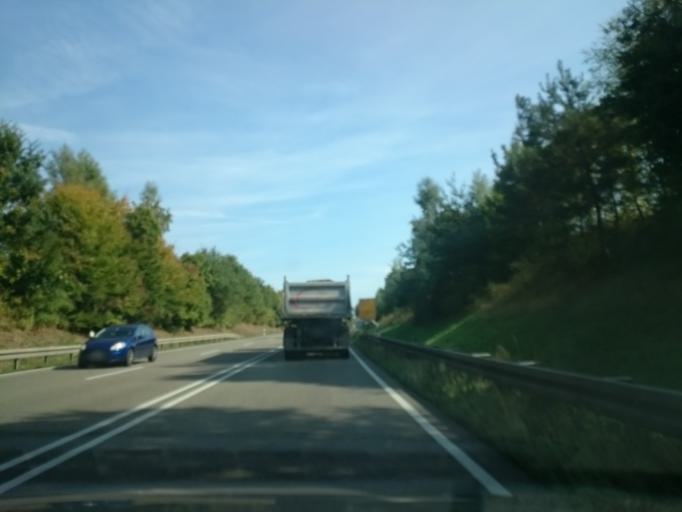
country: DE
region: Bavaria
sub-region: Upper Bavaria
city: Gachenbach
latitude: 48.5165
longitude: 11.2279
